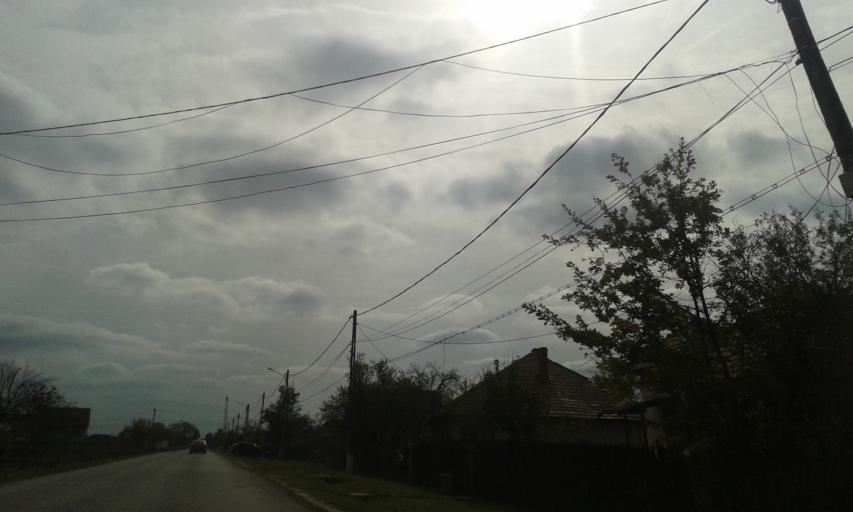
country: RO
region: Gorj
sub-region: Comuna Targu Carbunesti
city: Pojogeni
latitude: 44.9973
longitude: 23.4928
